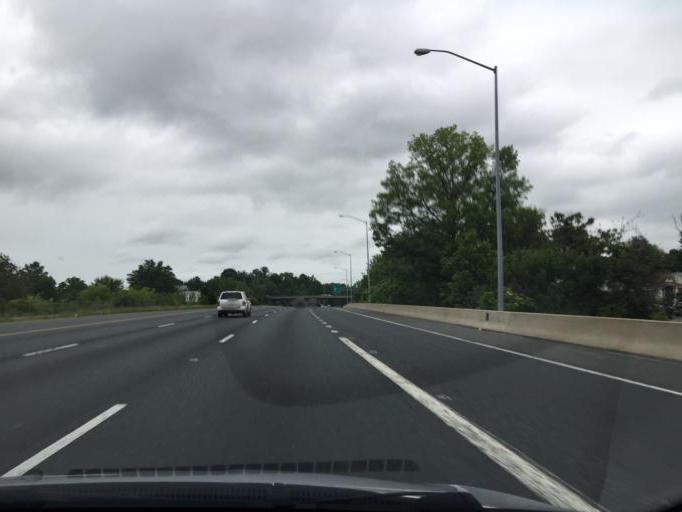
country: US
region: Maryland
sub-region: Baltimore County
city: Carney
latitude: 39.3822
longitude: -76.5217
